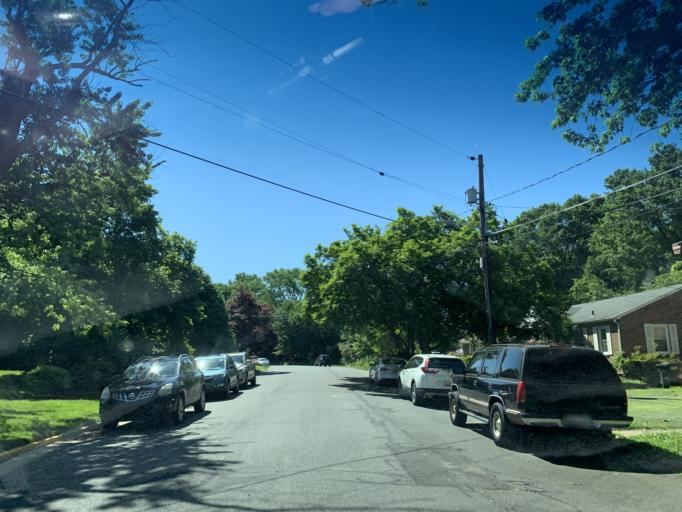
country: US
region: Maryland
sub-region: Harford County
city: Havre de Grace
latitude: 39.5388
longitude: -76.0970
